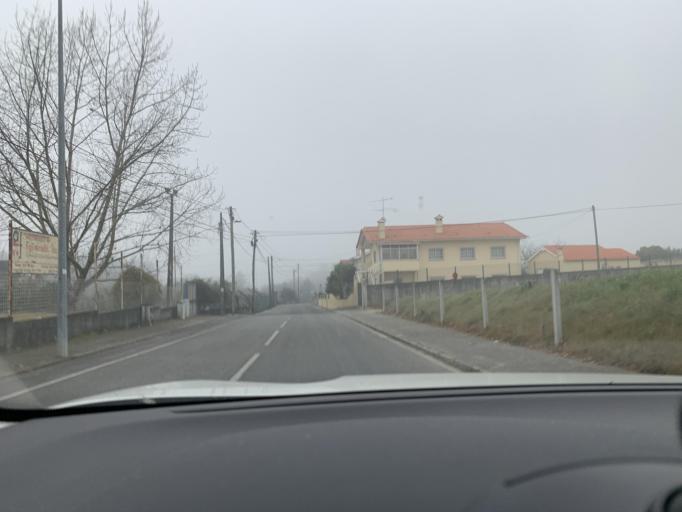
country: PT
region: Viseu
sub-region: Viseu
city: Viseu
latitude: 40.6357
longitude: -7.9192
